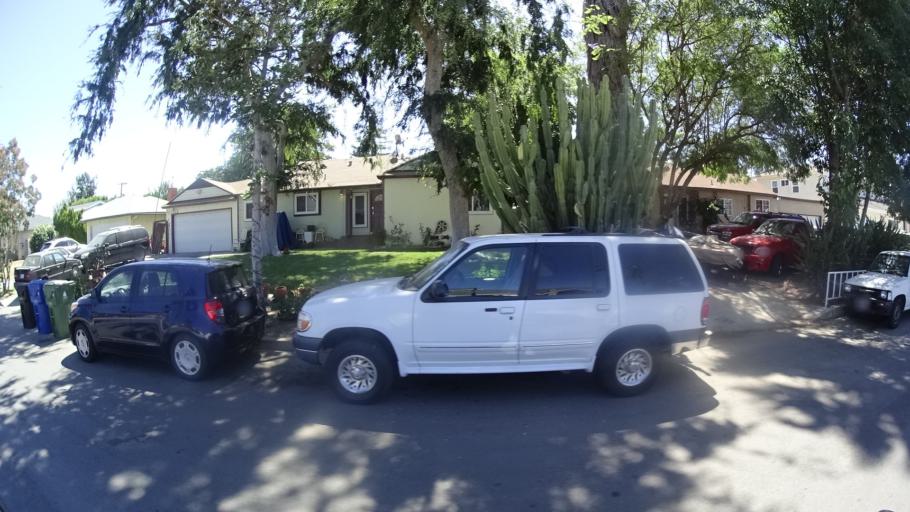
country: US
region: California
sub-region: Los Angeles County
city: Northridge
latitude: 34.1970
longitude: -118.4980
